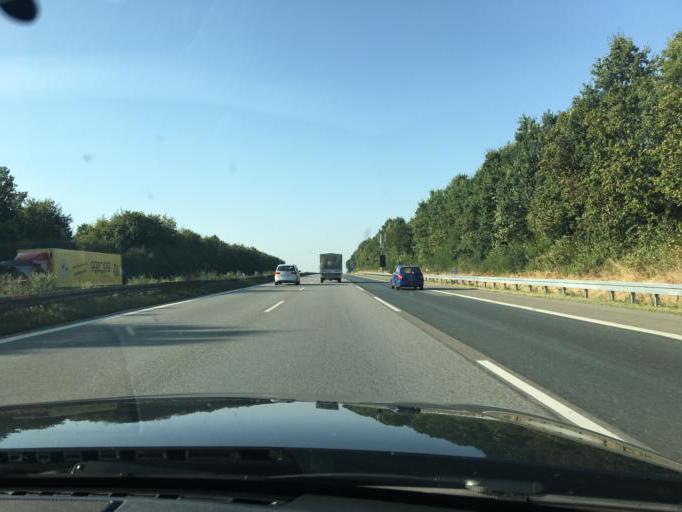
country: DE
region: Bavaria
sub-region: Regierungsbezirk Mittelfranken
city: Thalmassing
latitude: 49.1239
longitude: 11.2755
